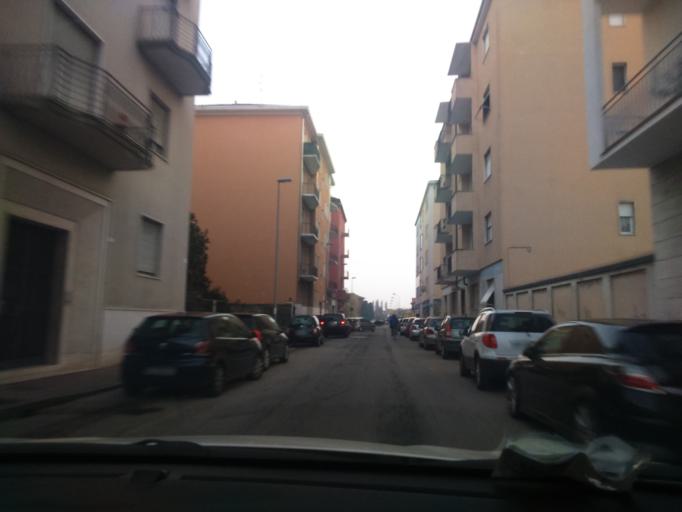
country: IT
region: Piedmont
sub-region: Provincia di Vercelli
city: Vercelli
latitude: 45.3194
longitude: 8.4166
